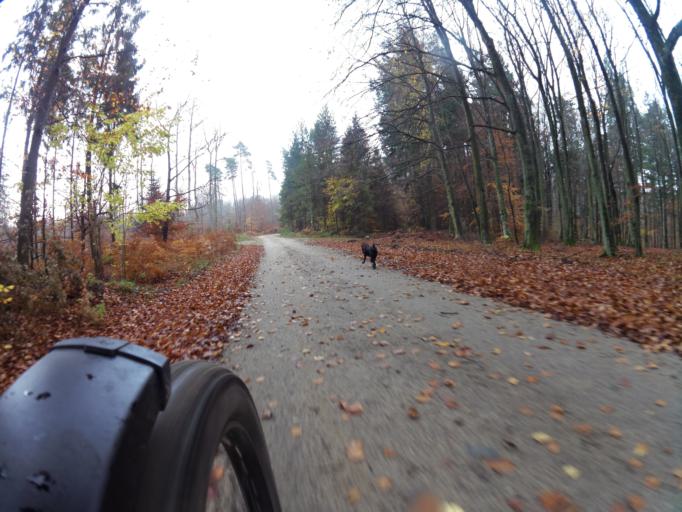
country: PL
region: Pomeranian Voivodeship
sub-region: Powiat pucki
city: Krokowa
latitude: 54.7690
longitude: 18.0945
